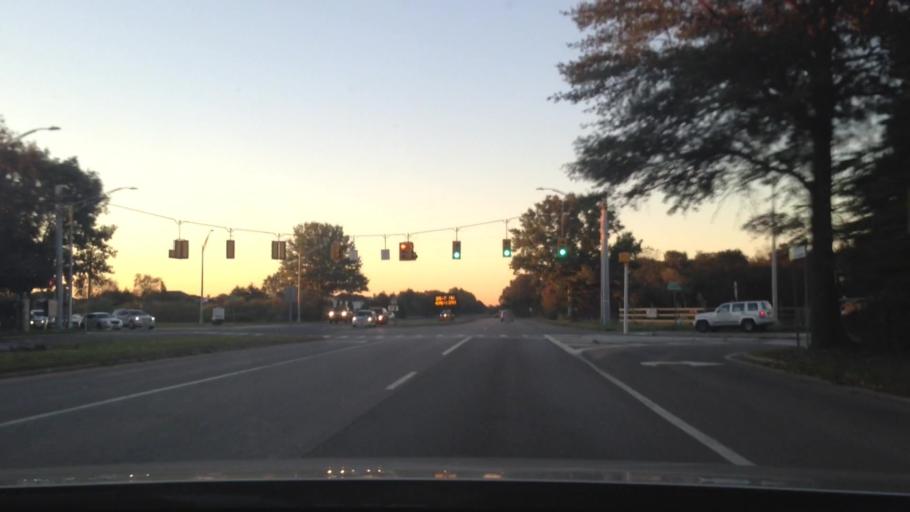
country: US
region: New York
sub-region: Suffolk County
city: Mount Sinai
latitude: 40.9337
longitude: -73.0092
